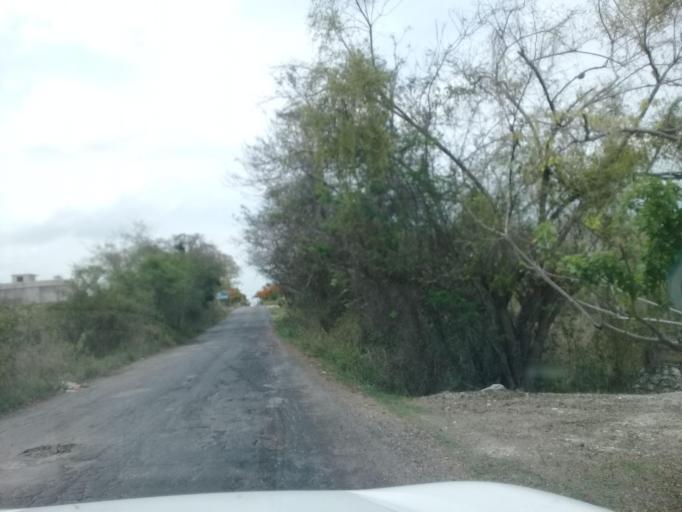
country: MX
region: Veracruz
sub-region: Emiliano Zapata
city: Plan del Rio
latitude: 19.3538
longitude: -96.6586
